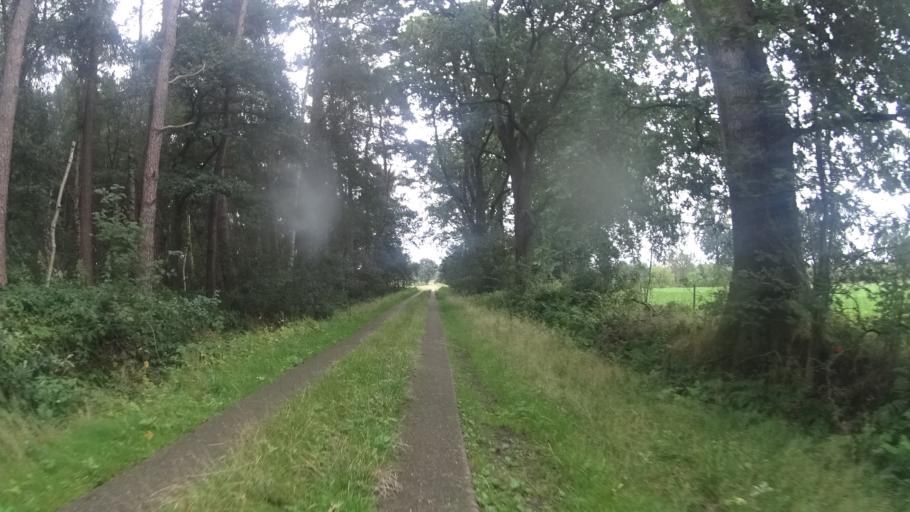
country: DE
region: Schleswig-Holstein
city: Heede
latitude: 53.7611
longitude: 9.7952
